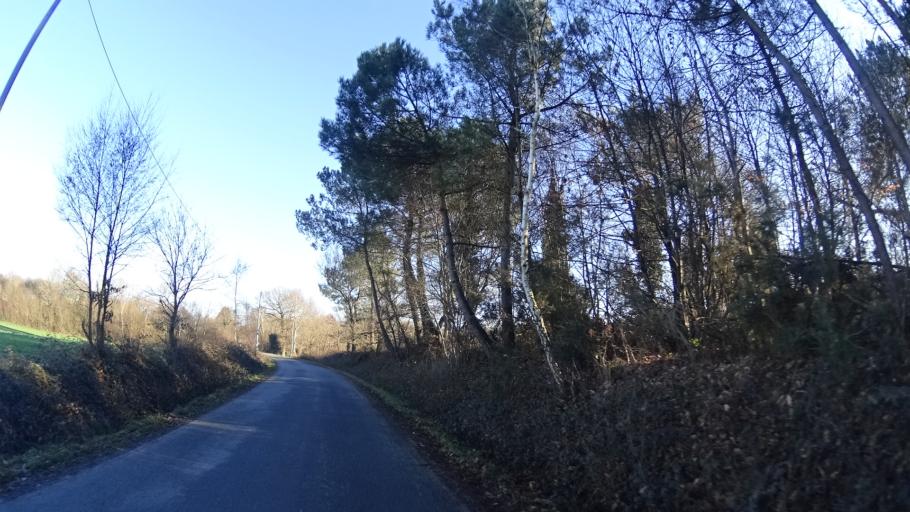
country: FR
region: Brittany
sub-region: Departement du Morbihan
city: Allaire
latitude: 47.6683
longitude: -2.1712
